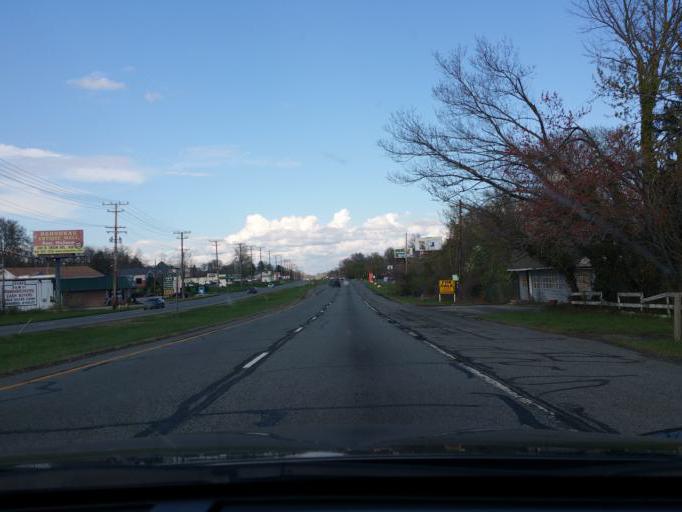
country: US
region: Maryland
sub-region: Harford County
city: Aberdeen
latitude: 39.5251
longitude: -76.1366
